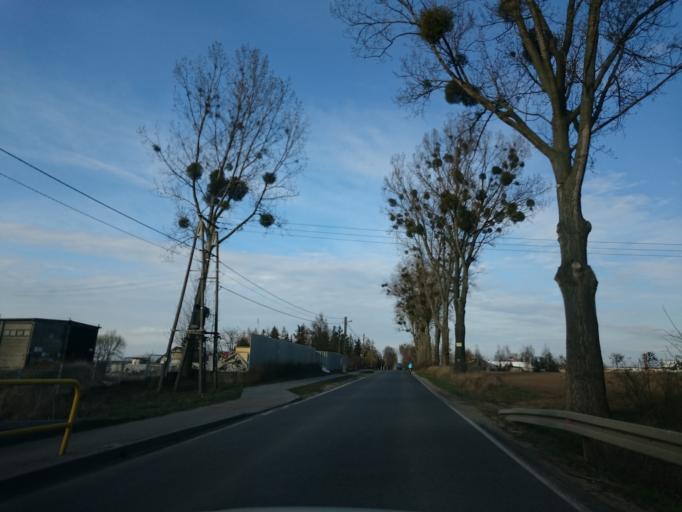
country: PL
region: Kujawsko-Pomorskie
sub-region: Powiat torunski
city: Lubicz Gorny
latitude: 53.0346
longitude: 18.7797
